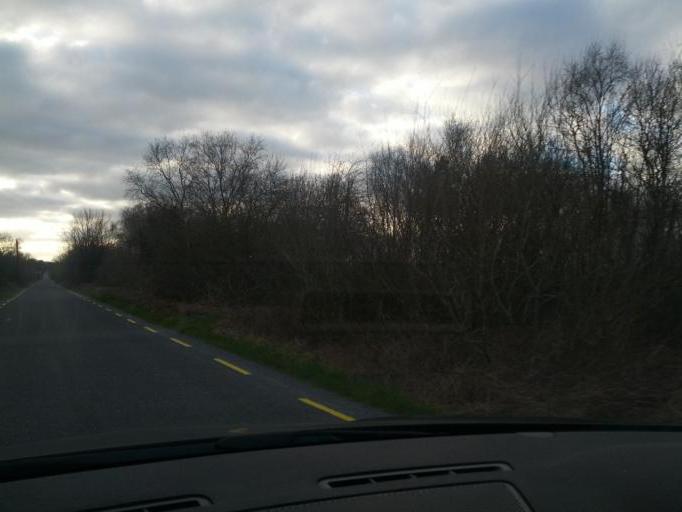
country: IE
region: Leinster
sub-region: An Iarmhi
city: Athlone
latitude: 53.3225
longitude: -7.9458
